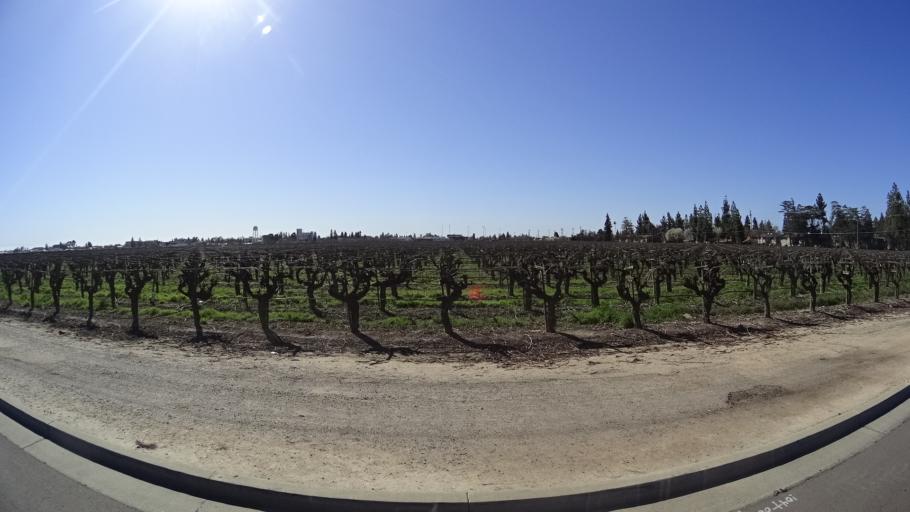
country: US
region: California
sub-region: Fresno County
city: Clovis
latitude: 36.8231
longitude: -119.7529
